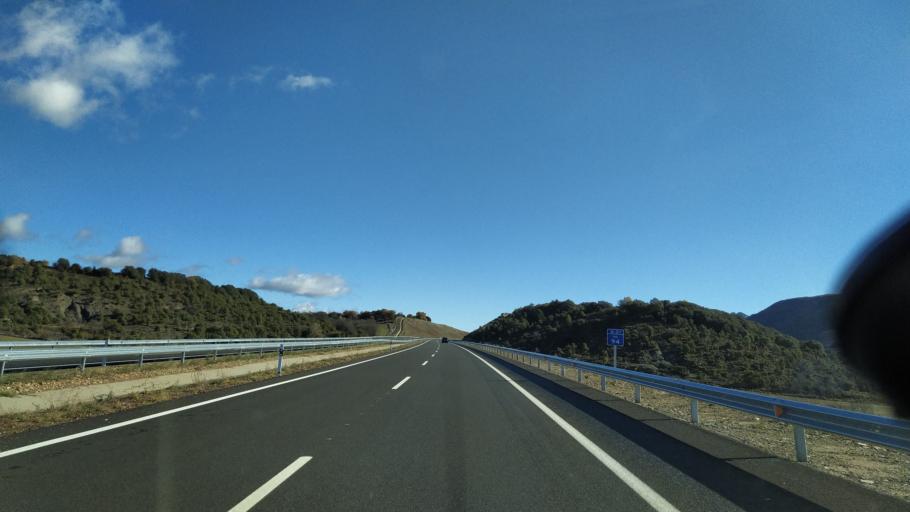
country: ES
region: Aragon
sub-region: Provincia de Huesca
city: Santa Cruz de la Seros
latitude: 42.5634
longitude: -0.6889
